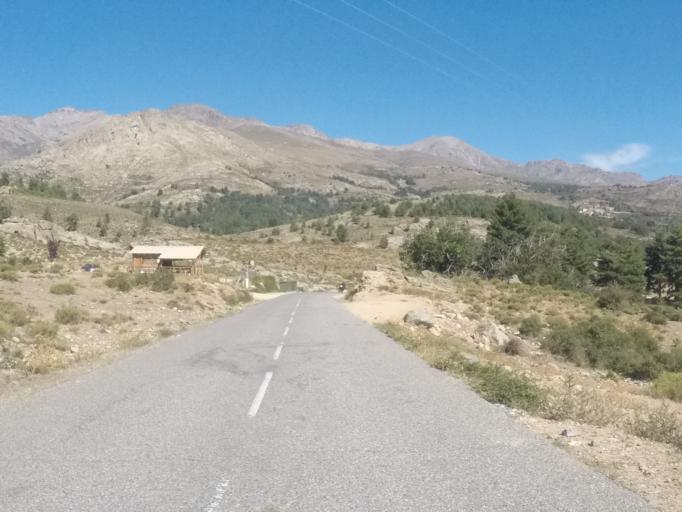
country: FR
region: Corsica
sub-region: Departement de la Haute-Corse
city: Corte
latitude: 42.3169
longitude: 8.9739
